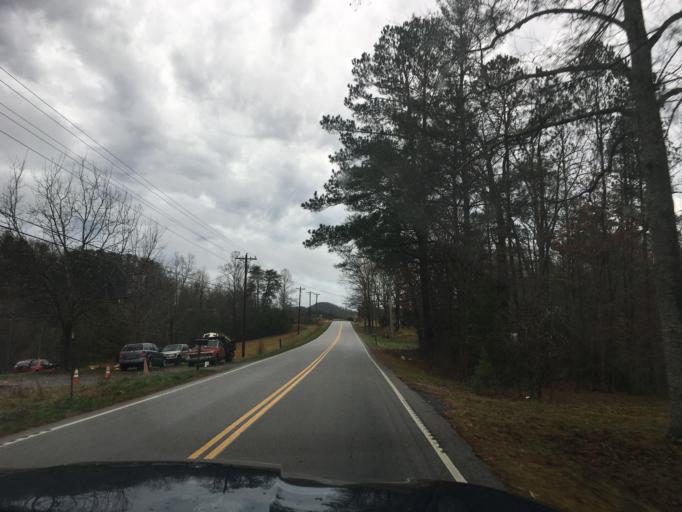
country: US
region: Tennessee
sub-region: Monroe County
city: Madisonville
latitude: 35.3651
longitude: -84.3224
